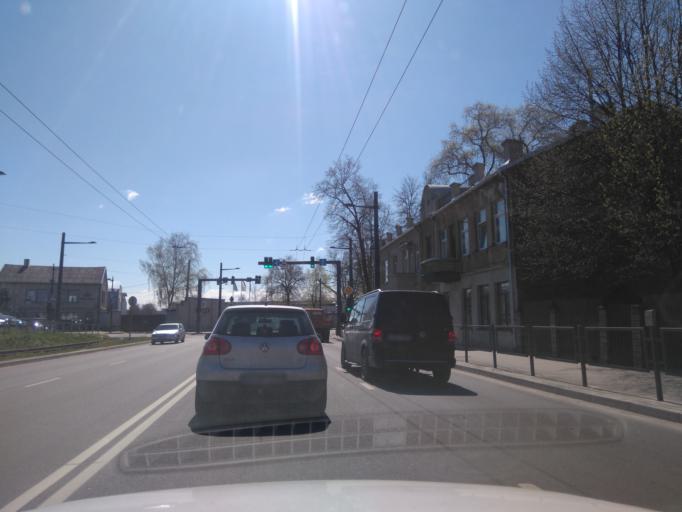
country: LT
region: Kauno apskritis
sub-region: Kaunas
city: Aleksotas
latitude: 54.8760
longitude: 23.9356
